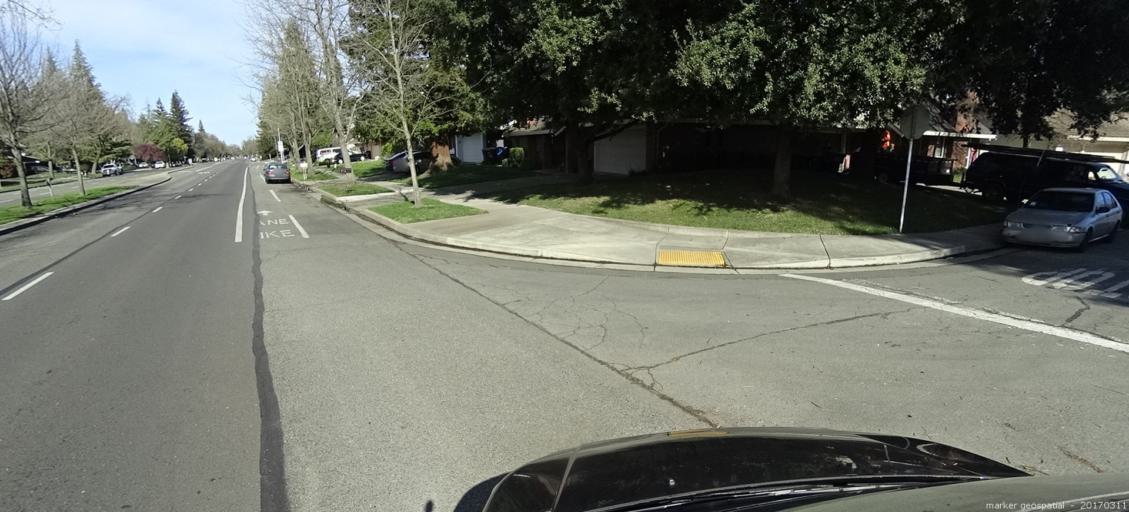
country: US
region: California
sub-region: Yolo County
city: West Sacramento
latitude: 38.4979
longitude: -121.5517
